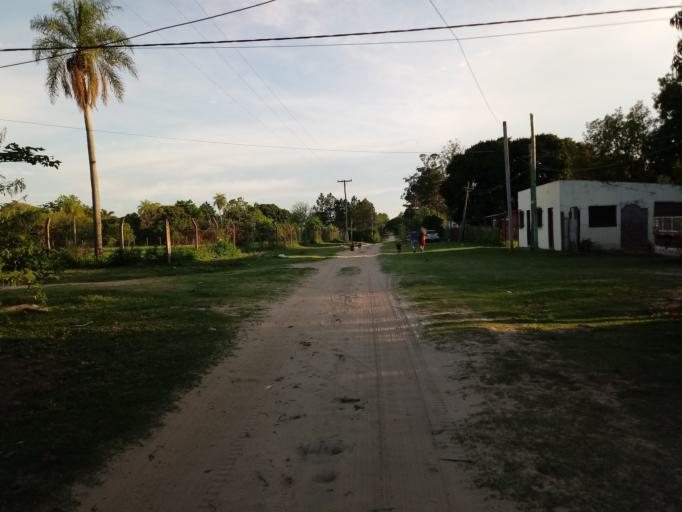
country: AR
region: Corrientes
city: San Luis del Palmar
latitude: -27.4519
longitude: -58.6573
